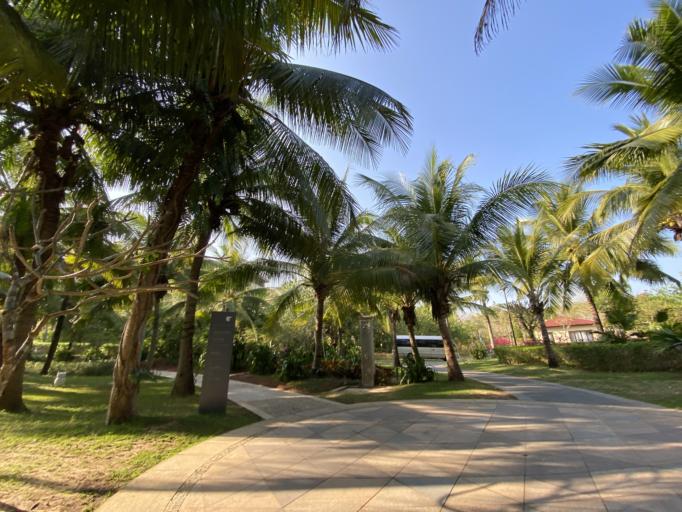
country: CN
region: Hainan
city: Haitangwan
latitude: 18.3493
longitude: 109.7396
